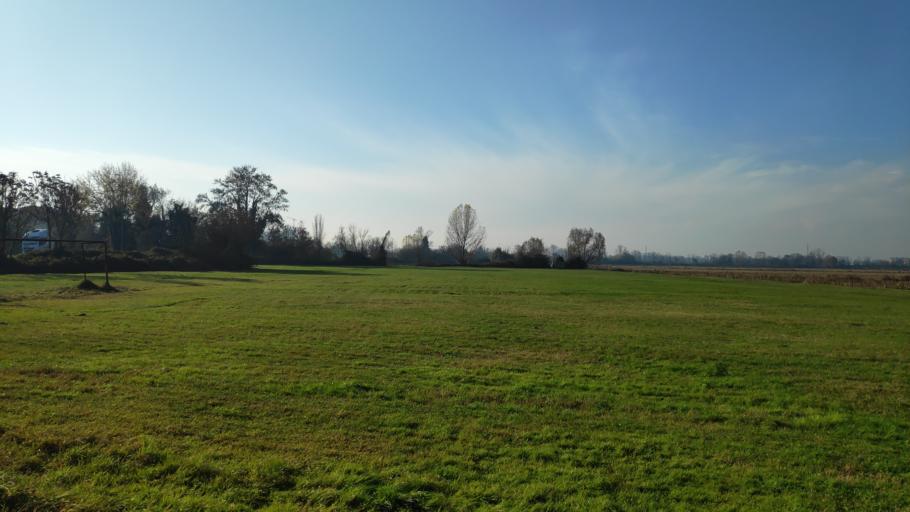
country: IT
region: Lombardy
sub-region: Citta metropolitana di Milano
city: Assago
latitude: 45.4238
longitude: 9.1564
